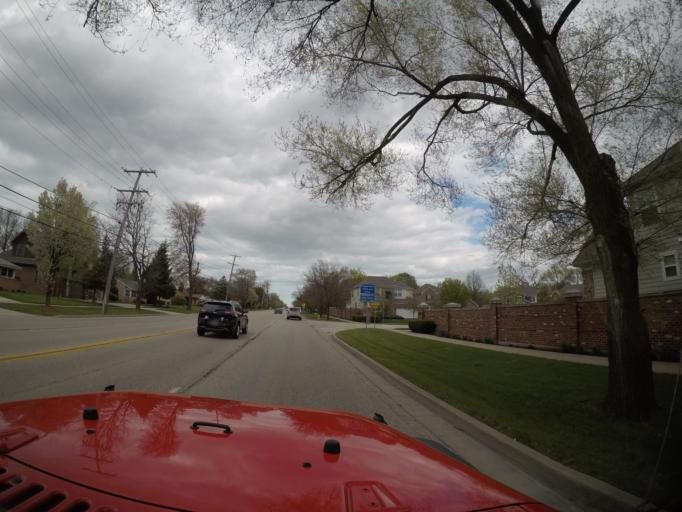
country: US
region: Illinois
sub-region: Cook County
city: Glenview
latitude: 42.0799
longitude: -87.7941
